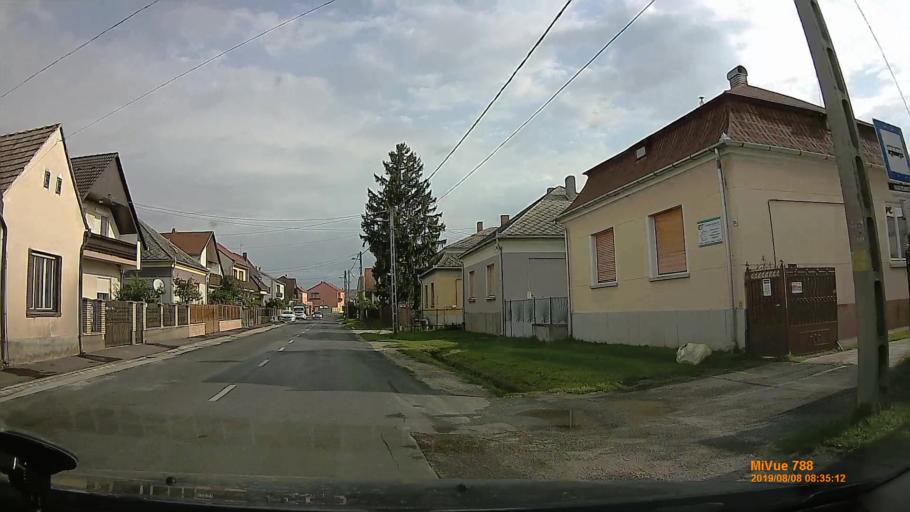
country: HU
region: Zala
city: Nagykanizsa
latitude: 46.4521
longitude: 16.9561
